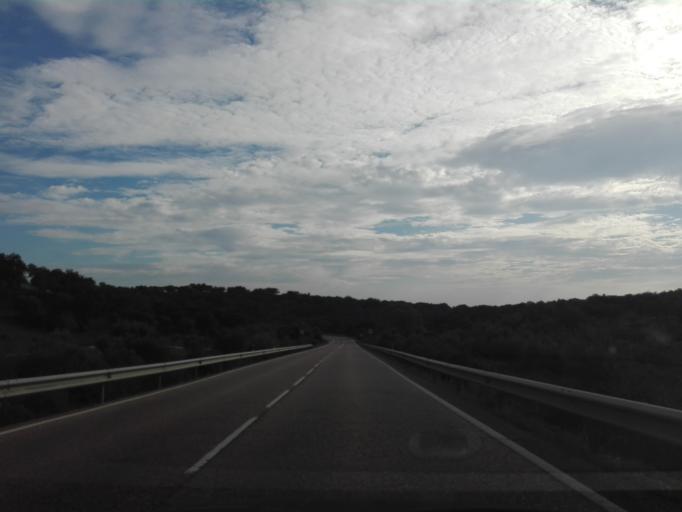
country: ES
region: Extremadura
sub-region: Provincia de Badajoz
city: Alburquerque
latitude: 39.1960
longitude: -6.9976
